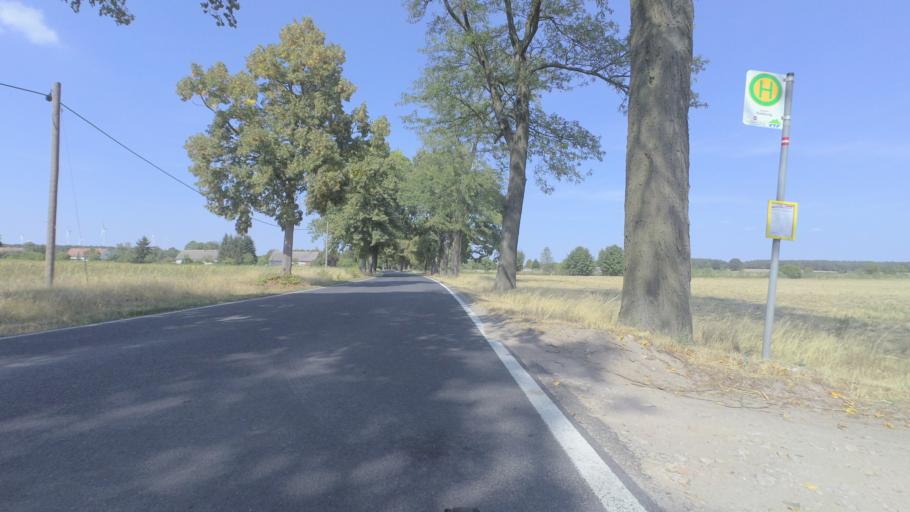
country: DE
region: Brandenburg
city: Sperenberg
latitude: 52.1849
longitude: 13.3232
